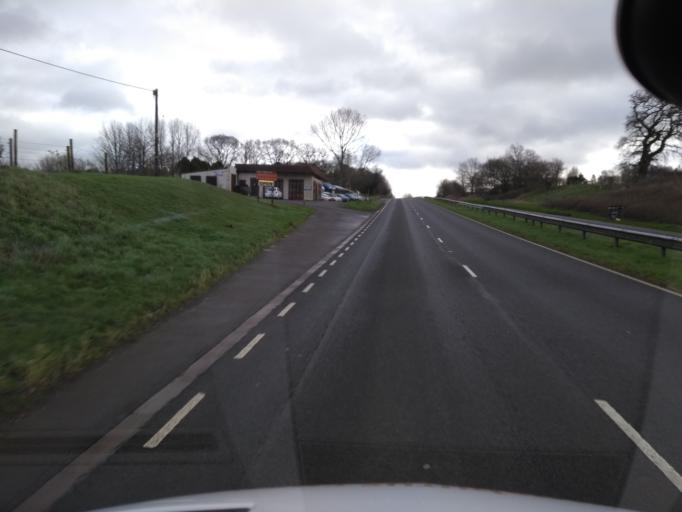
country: GB
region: England
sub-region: Somerset
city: Yeovil
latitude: 50.9446
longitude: -2.5802
